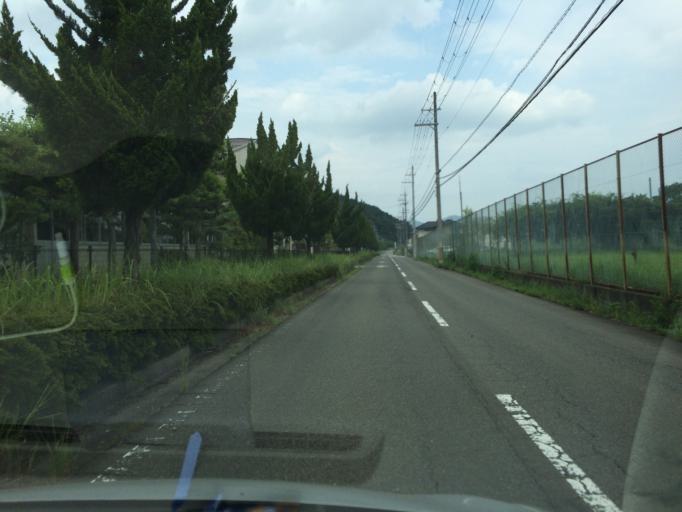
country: JP
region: Hyogo
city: Toyooka
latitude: 35.5149
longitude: 134.8172
